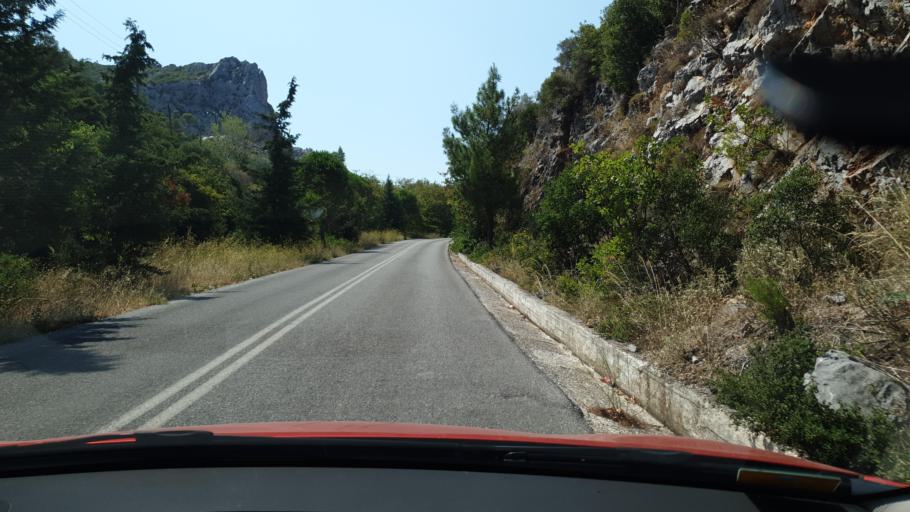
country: GR
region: Central Greece
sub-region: Nomos Evvoias
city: Kymi
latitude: 38.6297
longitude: 24.1016
